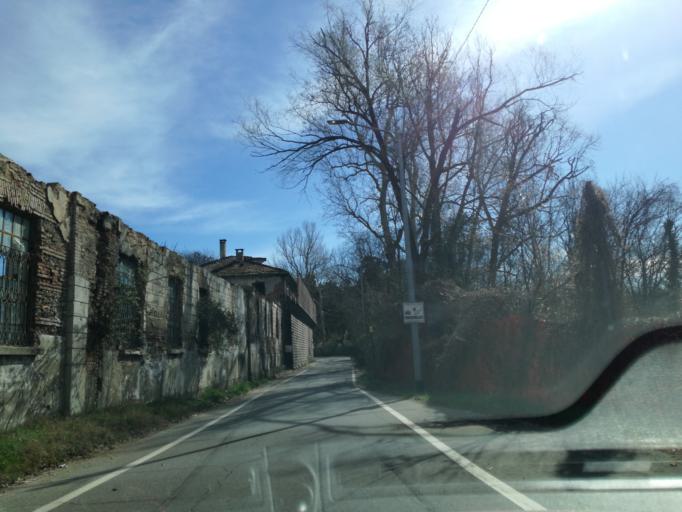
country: IT
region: Lombardy
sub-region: Provincia di Monza e Brianza
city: Lesmo
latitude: 45.6348
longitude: 9.2998
